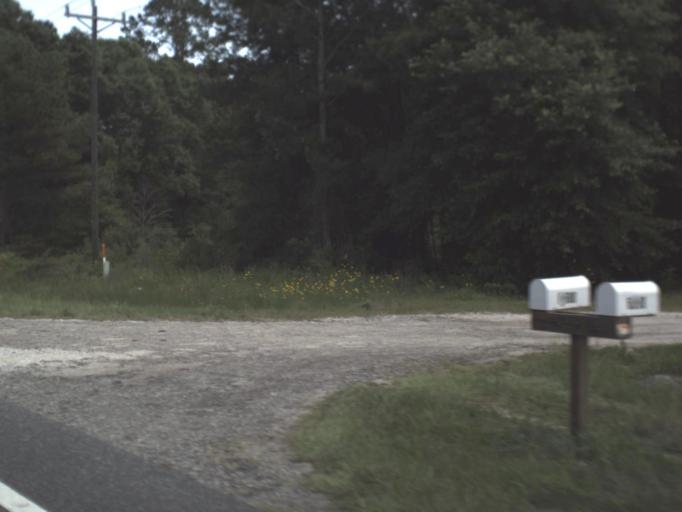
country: US
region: Florida
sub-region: Taylor County
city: Perry
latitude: 30.0321
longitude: -83.5423
